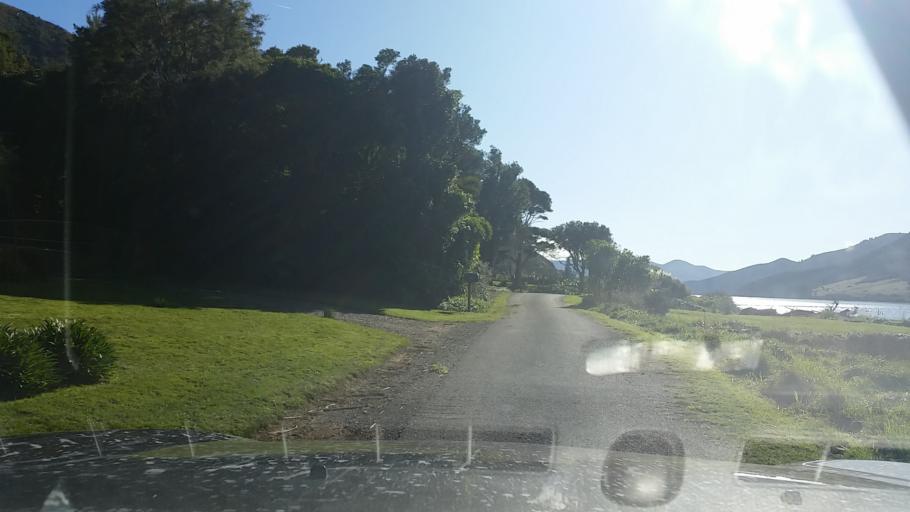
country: NZ
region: Marlborough
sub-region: Marlborough District
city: Picton
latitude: -41.1133
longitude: 174.0350
